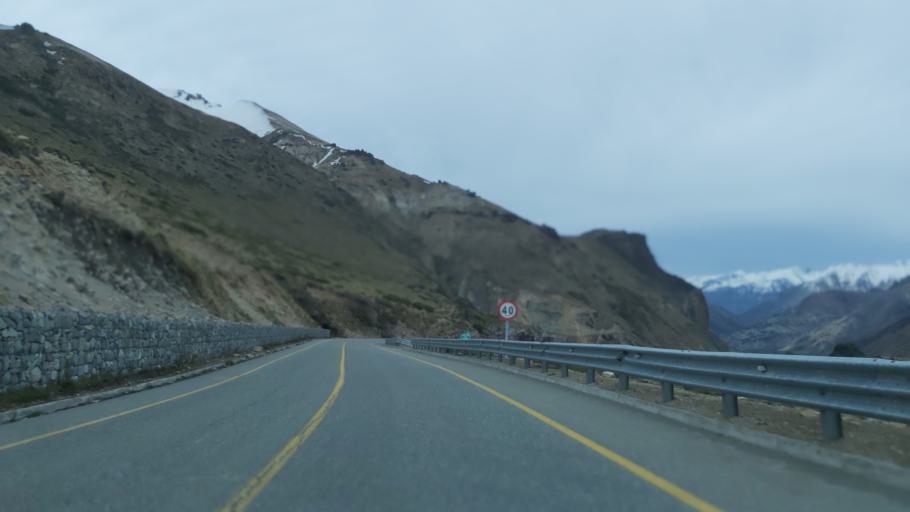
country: CL
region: Maule
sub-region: Provincia de Linares
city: Colbun
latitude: -35.9540
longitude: -70.5907
